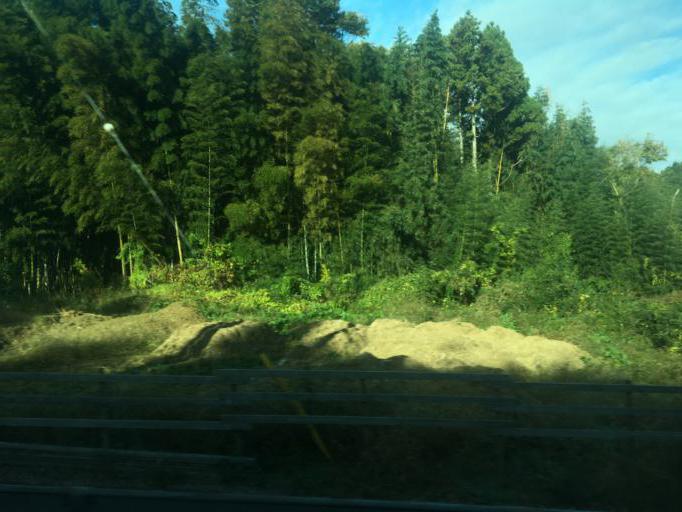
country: JP
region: Ibaraki
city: Ushiku
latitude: 36.0028
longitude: 140.1555
